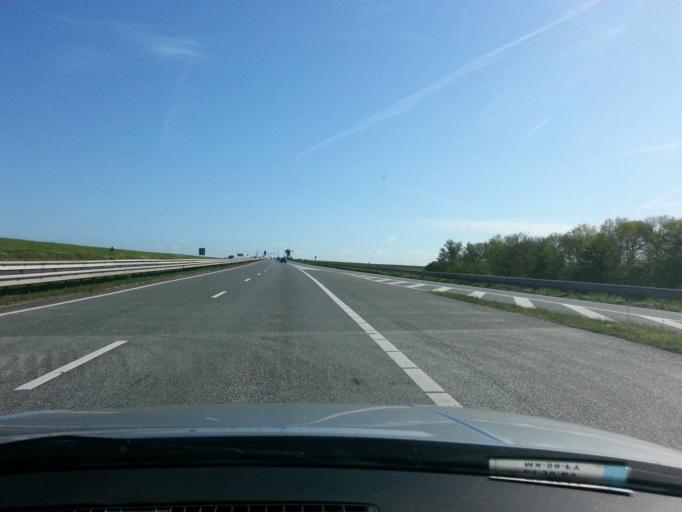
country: NL
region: Flevoland
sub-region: Gemeente Urk
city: Urk
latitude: 52.6055
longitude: 5.6320
